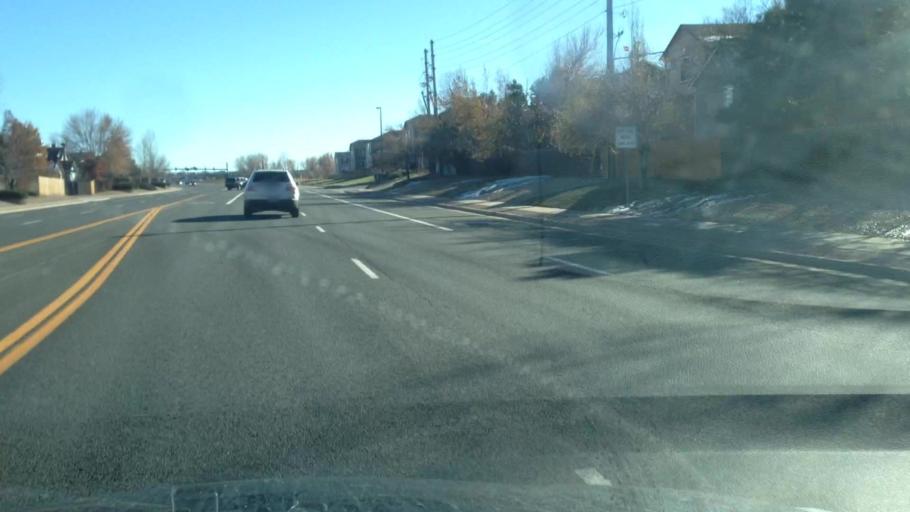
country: US
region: Colorado
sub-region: Douglas County
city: Stonegate
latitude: 39.5581
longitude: -104.7956
